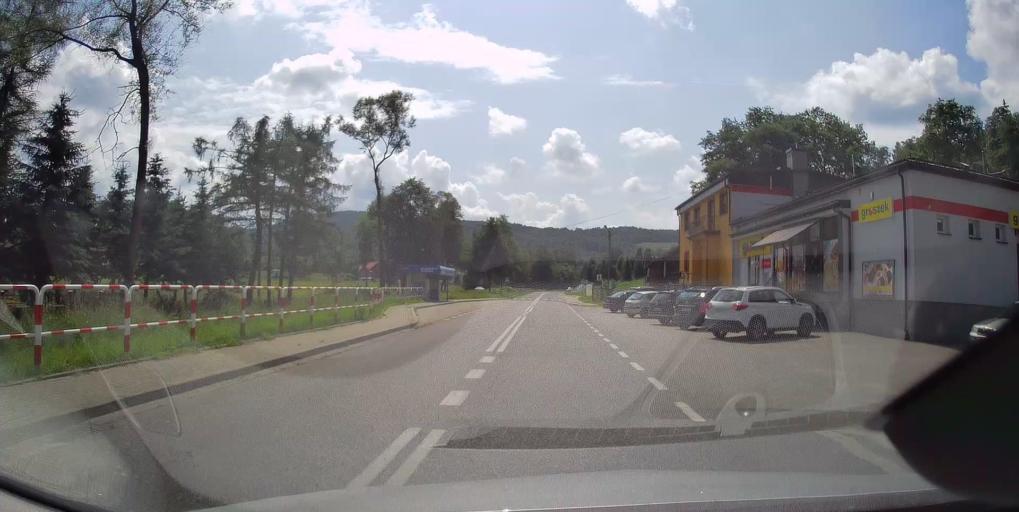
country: PL
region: Lesser Poland Voivodeship
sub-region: Powiat tarnowski
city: Zakliczyn
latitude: 49.7981
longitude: 20.7976
